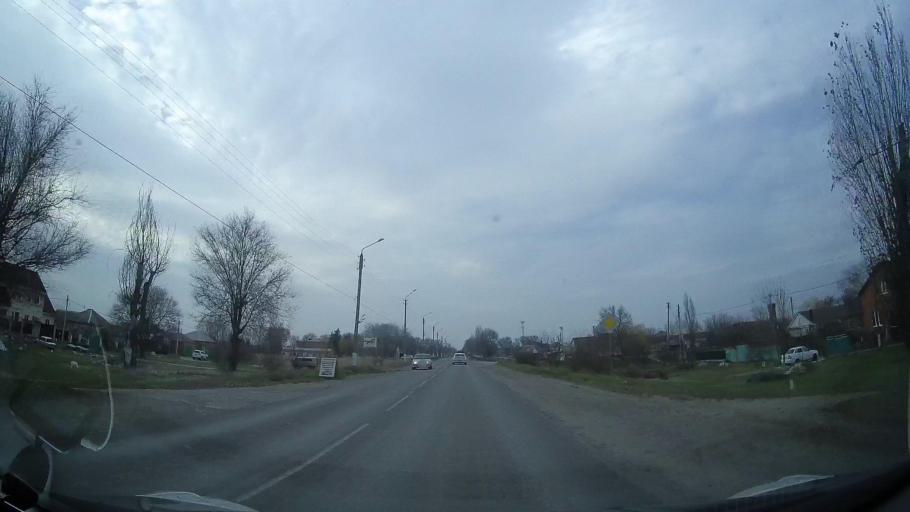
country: RU
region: Rostov
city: Ol'ginskaya
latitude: 47.1848
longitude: 39.9555
